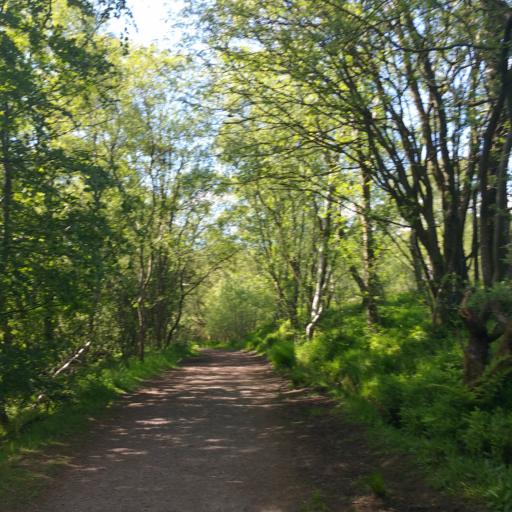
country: GB
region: Scotland
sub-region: East Dunbartonshire
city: Milngavie
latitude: 55.9545
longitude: -4.3251
